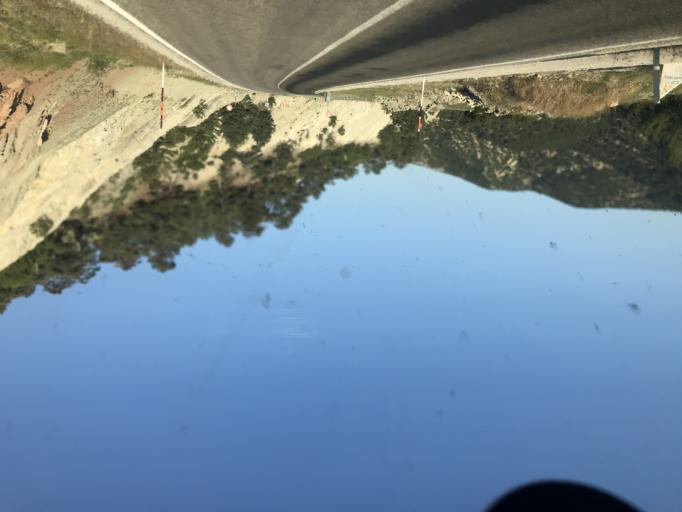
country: TR
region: Antalya
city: Korkuteli
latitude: 37.1353
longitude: 30.0681
